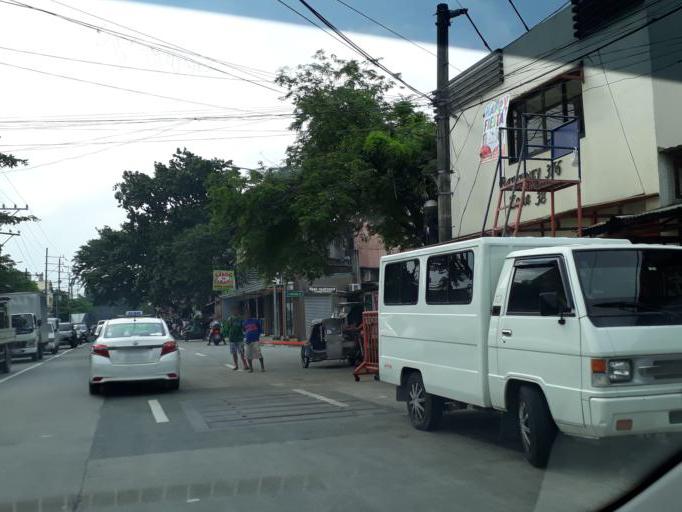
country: PH
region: Metro Manila
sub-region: City of Manila
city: Manila
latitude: 14.6270
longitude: 120.9861
